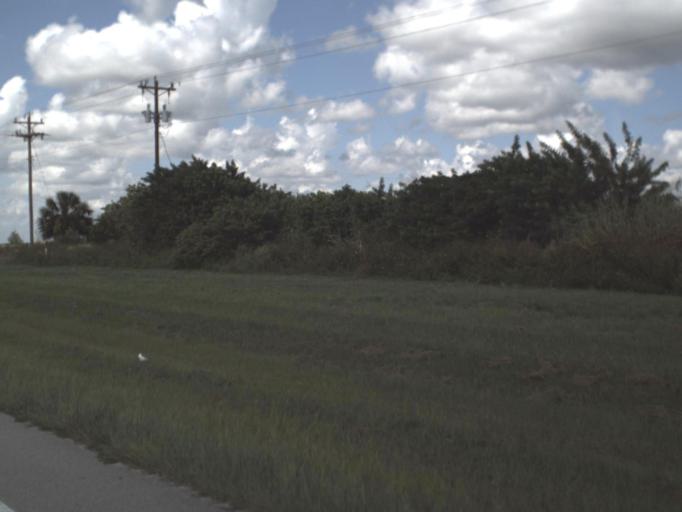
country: US
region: Florida
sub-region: Collier County
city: Immokalee
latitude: 26.4896
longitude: -81.4502
